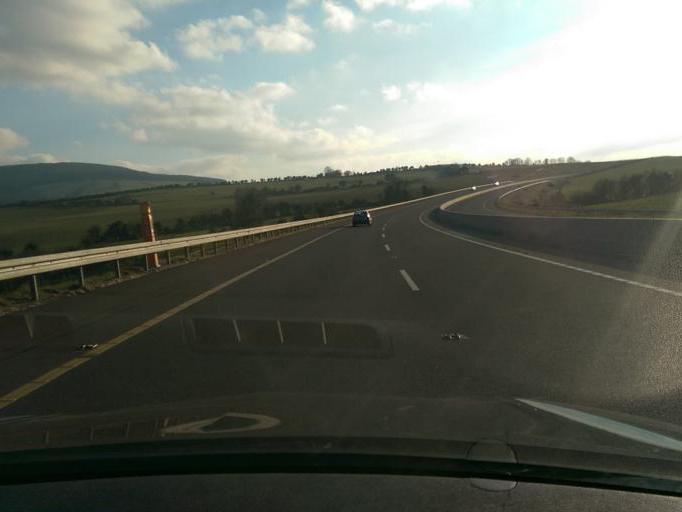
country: IE
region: Munster
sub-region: North Tipperary
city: Templemore
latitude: 52.8891
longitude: -7.9142
